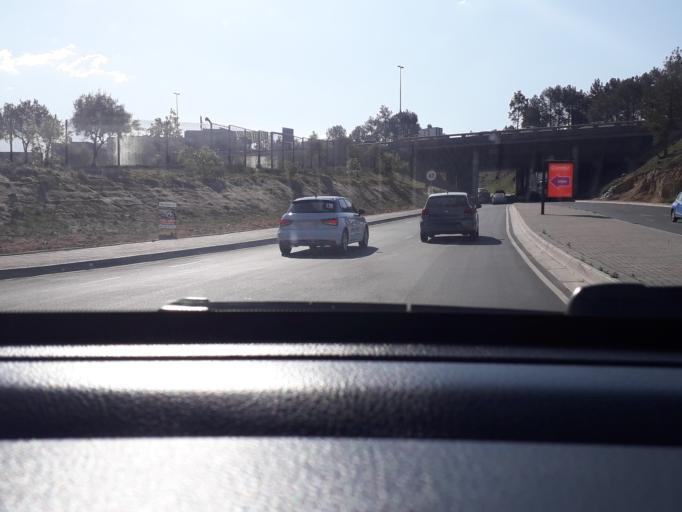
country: ZA
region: Gauteng
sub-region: City of Johannesburg Metropolitan Municipality
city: Midrand
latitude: -26.0424
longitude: 28.1050
